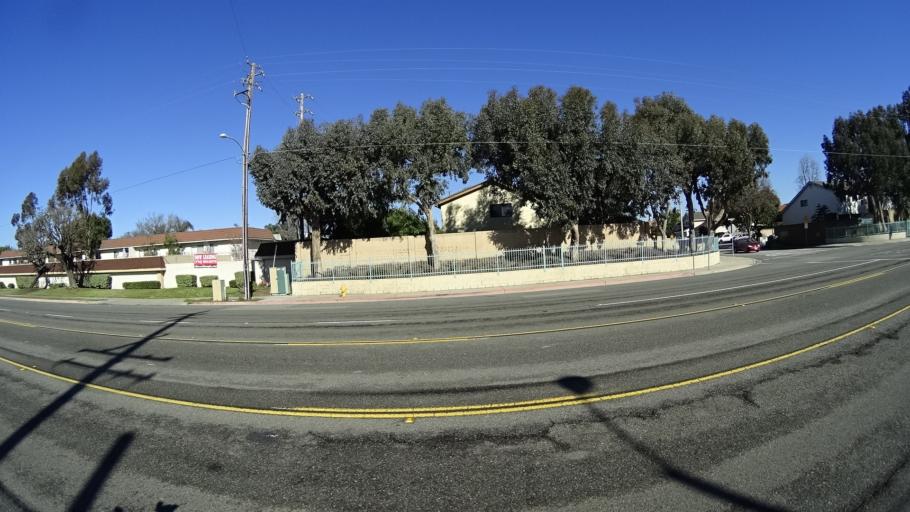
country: US
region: California
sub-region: Orange County
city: Placentia
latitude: 33.8642
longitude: -117.8651
